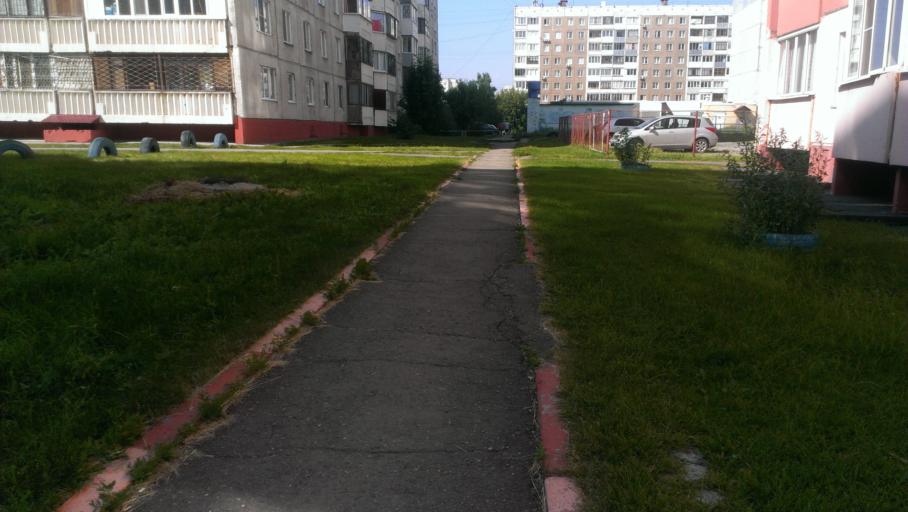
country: RU
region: Altai Krai
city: Novosilikatnyy
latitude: 53.3378
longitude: 83.6724
